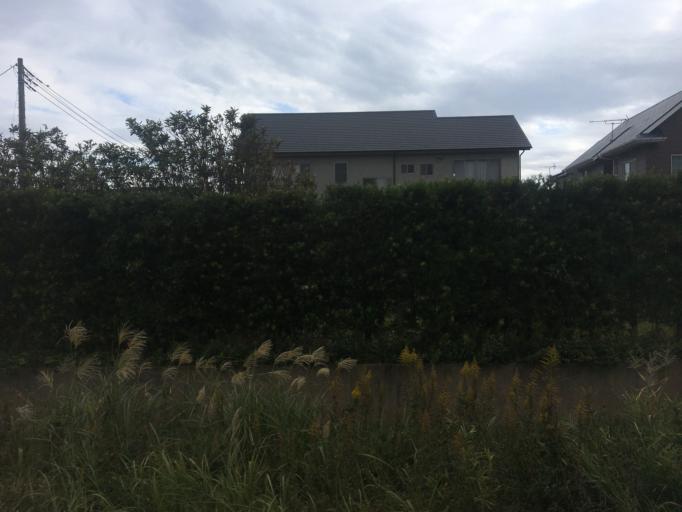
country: JP
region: Chiba
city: Tateyama
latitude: 35.0205
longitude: 139.9777
